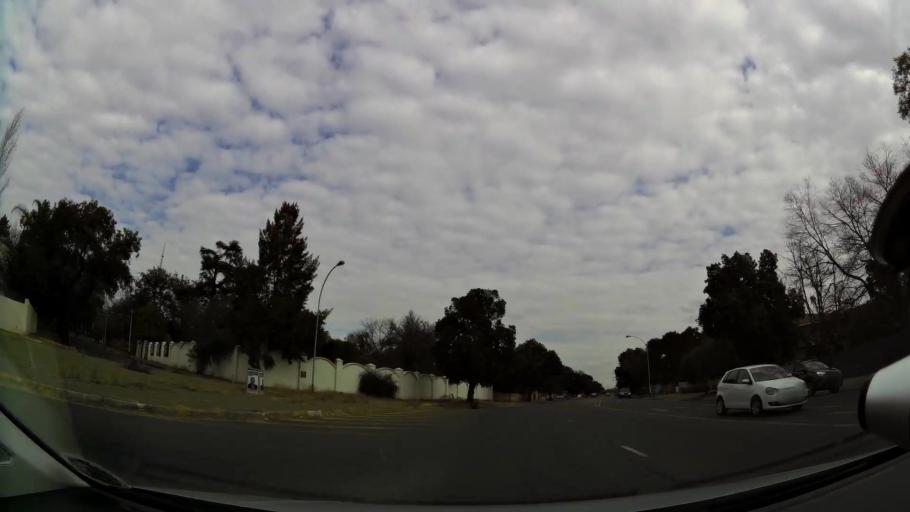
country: ZA
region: Orange Free State
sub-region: Mangaung Metropolitan Municipality
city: Bloemfontein
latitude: -29.0950
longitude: 26.2264
